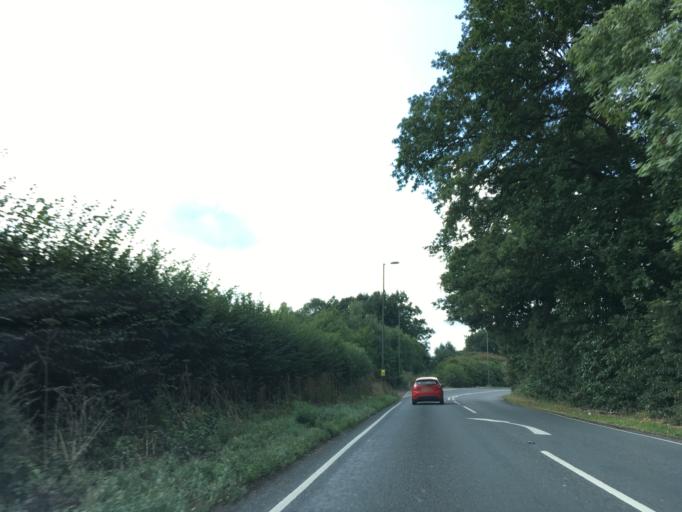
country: GB
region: England
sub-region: Hampshire
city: Highclere
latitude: 51.3488
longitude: -1.3368
